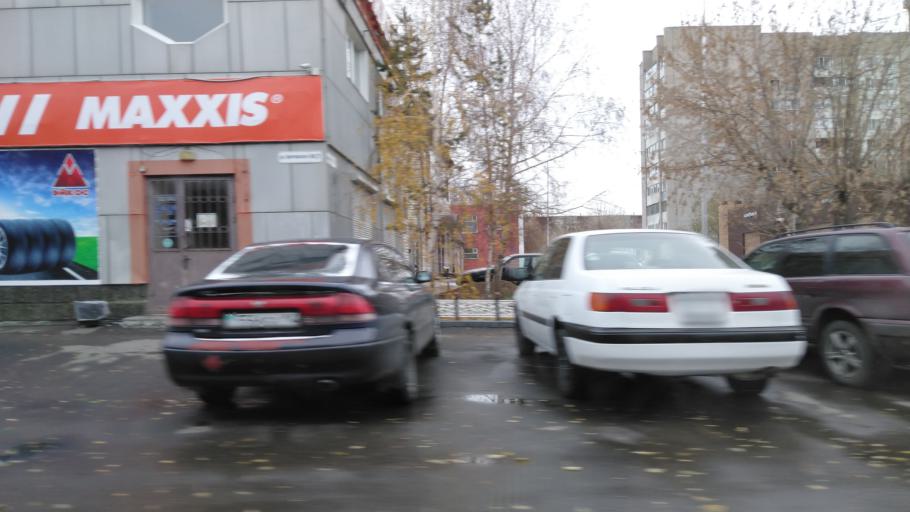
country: KZ
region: Pavlodar
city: Pavlodar
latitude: 52.2776
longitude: 76.9620
